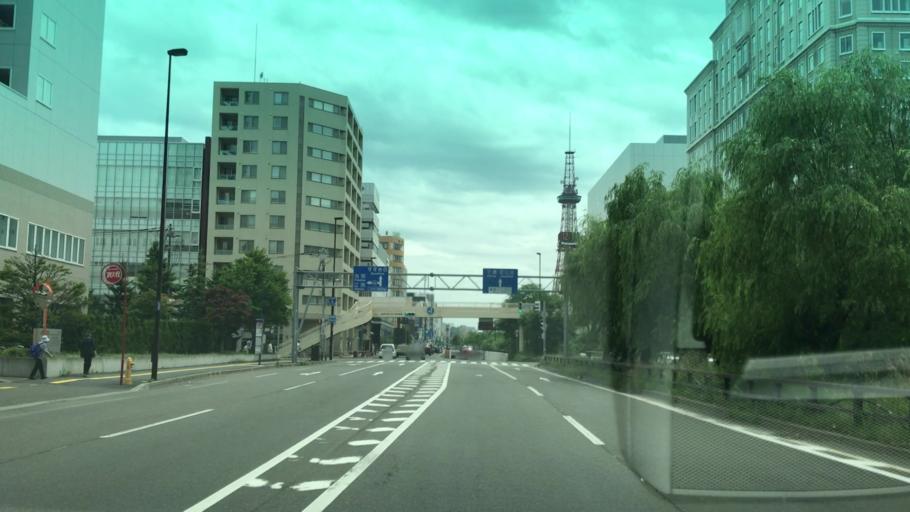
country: JP
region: Hokkaido
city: Sapporo
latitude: 43.0658
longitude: 141.3560
